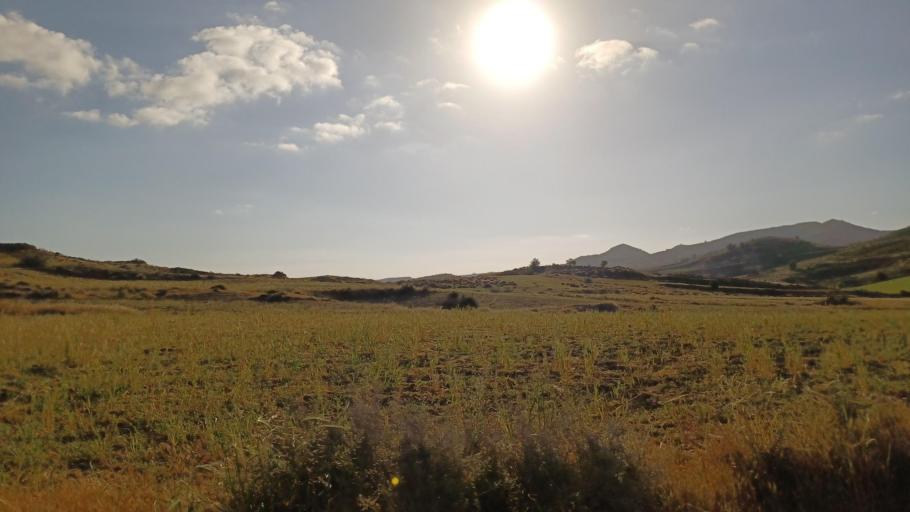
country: CY
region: Lefkosia
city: Peristerona
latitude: 35.0722
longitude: 33.0443
